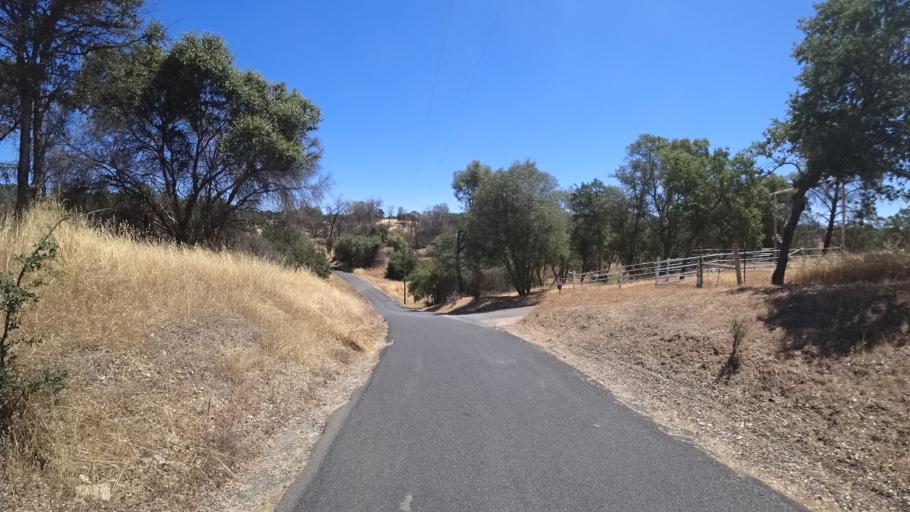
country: US
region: California
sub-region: Calaveras County
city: Copperopolis
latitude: 37.9650
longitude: -120.6958
